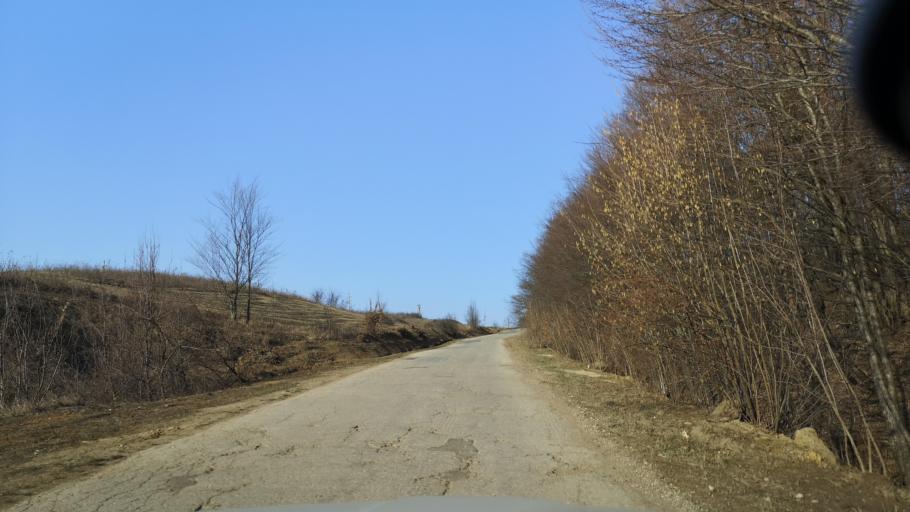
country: MD
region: Nisporeni
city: Nisporeni
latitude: 47.0995
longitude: 28.3152
